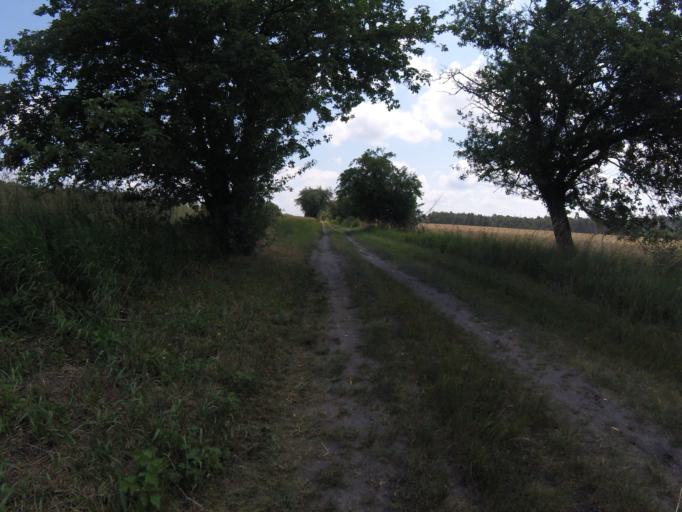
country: DE
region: Brandenburg
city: Bestensee
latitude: 52.2668
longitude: 13.7028
